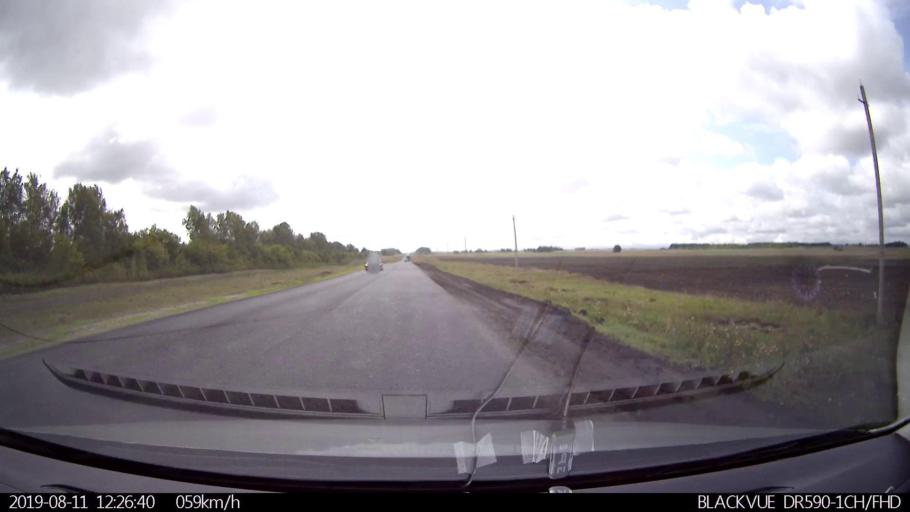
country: RU
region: Ulyanovsk
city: Ignatovka
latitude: 53.8621
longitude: 47.9286
